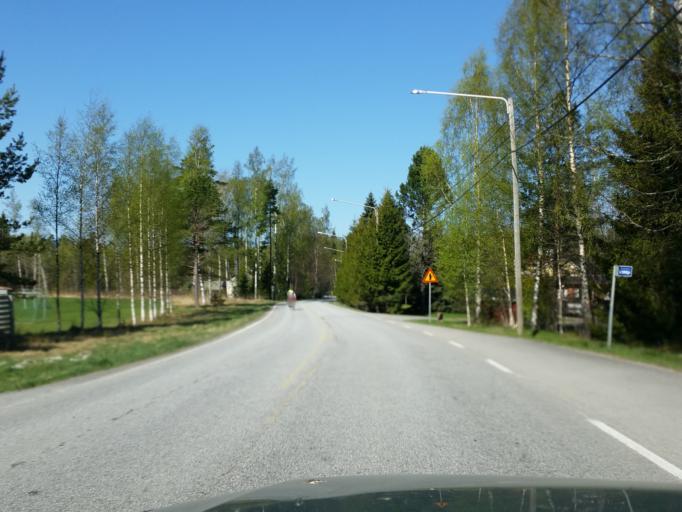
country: FI
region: Uusimaa
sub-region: Helsinki
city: Lohja
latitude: 60.1740
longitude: 24.1192
